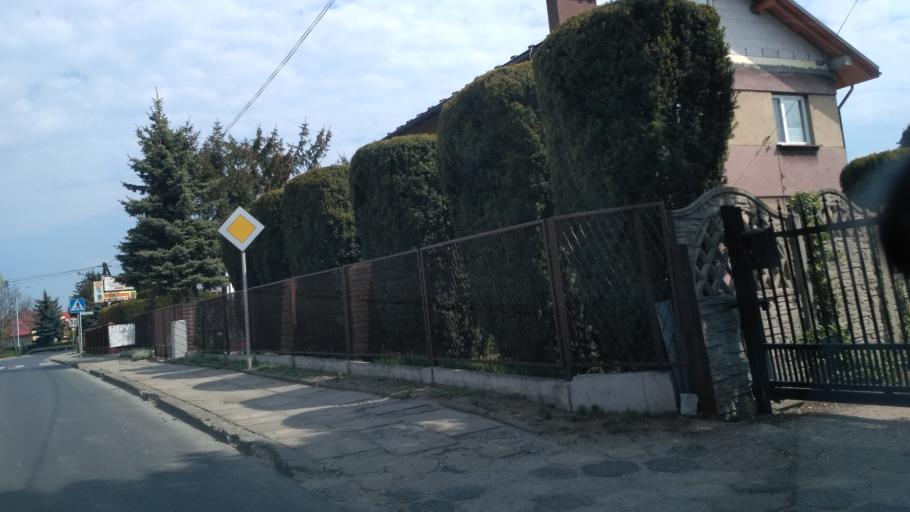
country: PL
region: Subcarpathian Voivodeship
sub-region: Powiat jaroslawski
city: Jaroslaw
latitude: 50.0257
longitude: 22.6729
